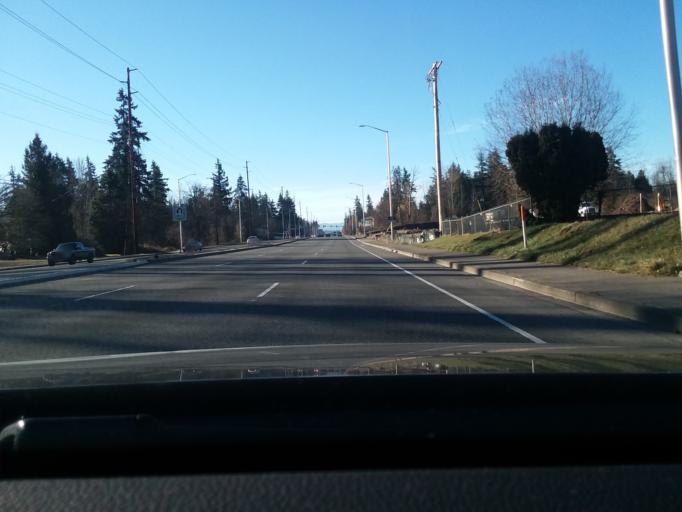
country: US
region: Washington
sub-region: Pierce County
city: Frederickson
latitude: 47.1211
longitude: -122.3577
